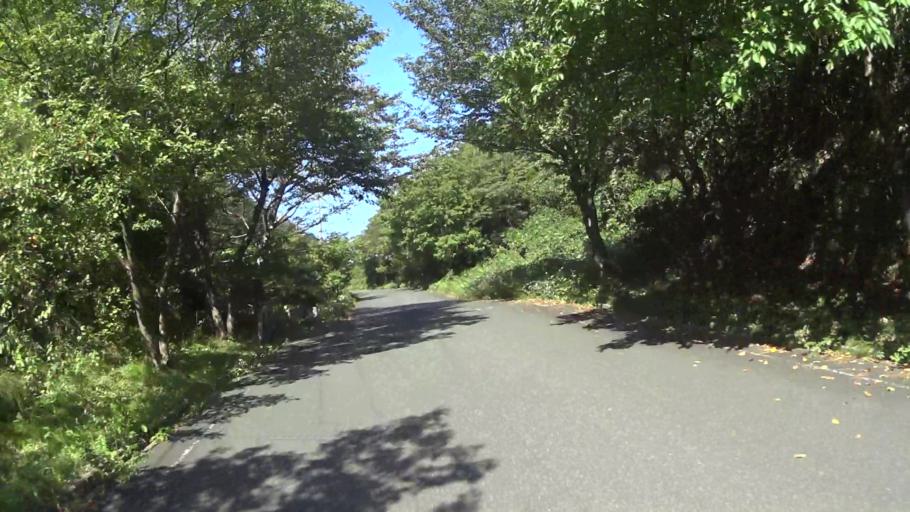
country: JP
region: Kyoto
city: Miyazu
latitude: 35.7723
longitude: 135.2254
